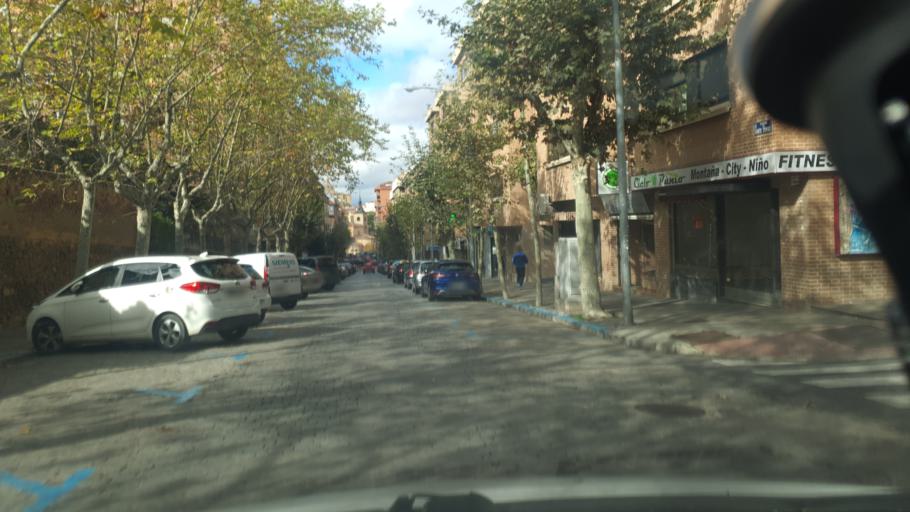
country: ES
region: Castille and Leon
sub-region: Provincia de Segovia
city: Segovia
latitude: 40.9429
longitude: -4.1180
